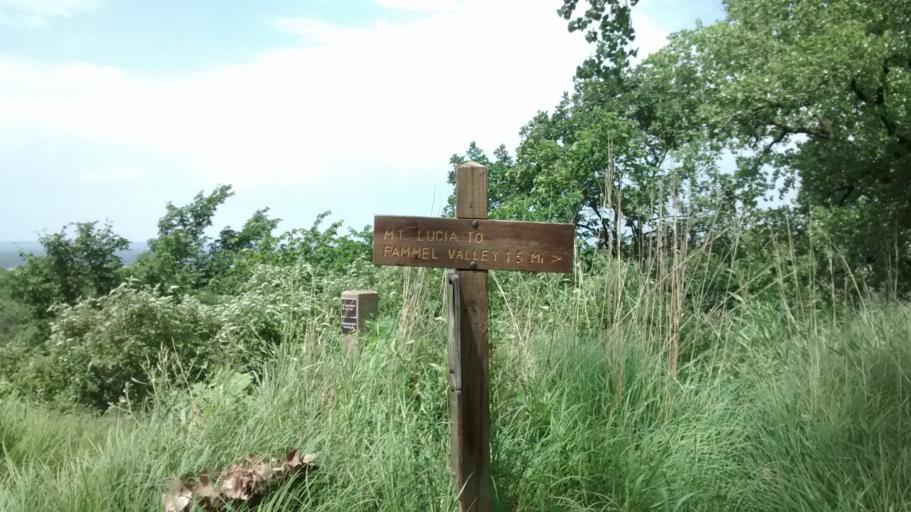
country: US
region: South Dakota
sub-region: Union County
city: North Sioux City
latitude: 42.5410
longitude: -96.4647
